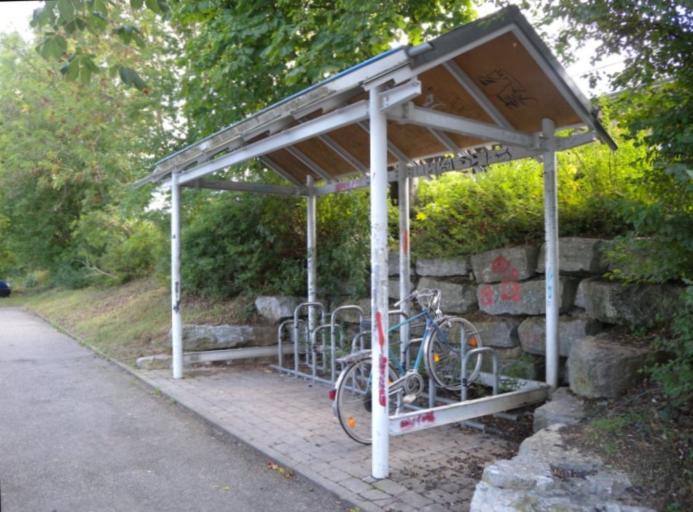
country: DE
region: Baden-Wuerttemberg
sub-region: Regierungsbezirk Stuttgart
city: Sersheim
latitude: 48.9615
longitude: 9.0629
